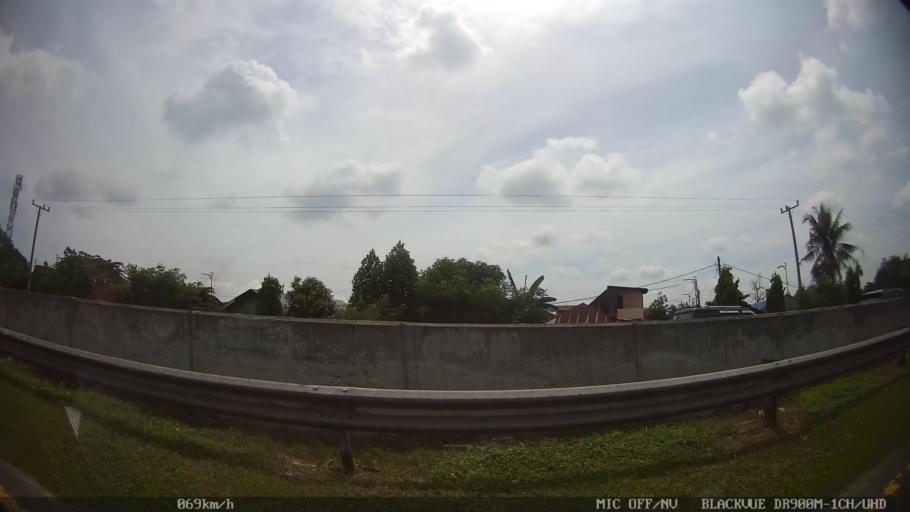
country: ID
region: North Sumatra
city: Labuhan Deli
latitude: 3.6626
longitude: 98.6823
